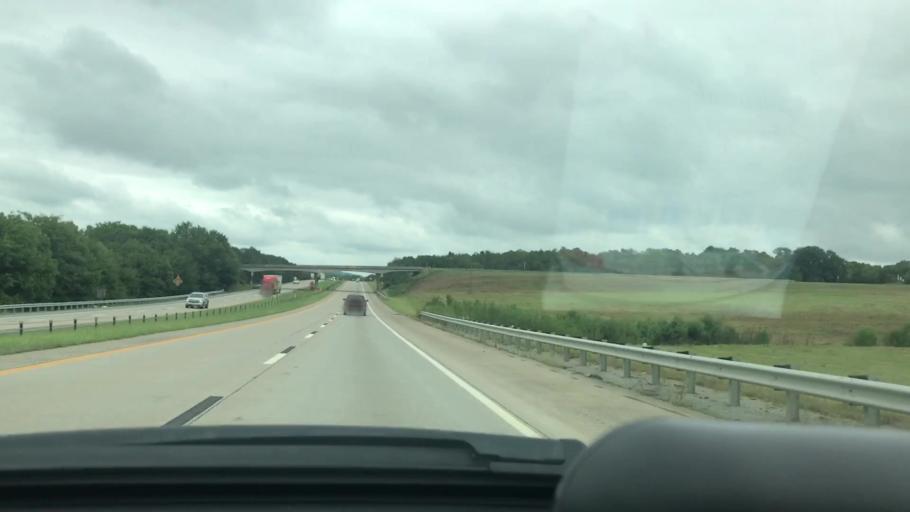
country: US
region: Oklahoma
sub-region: Pittsburg County
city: Krebs
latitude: 34.9978
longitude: -95.7205
